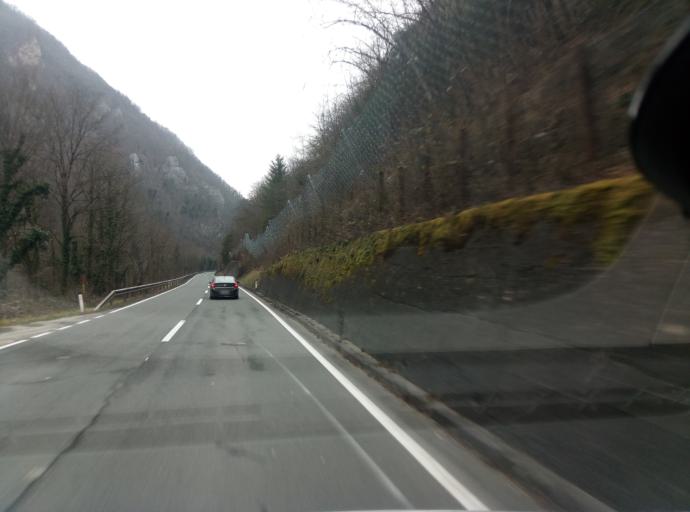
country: SI
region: Zagorje ob Savi
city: Kisovec
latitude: 46.1081
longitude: 14.9696
